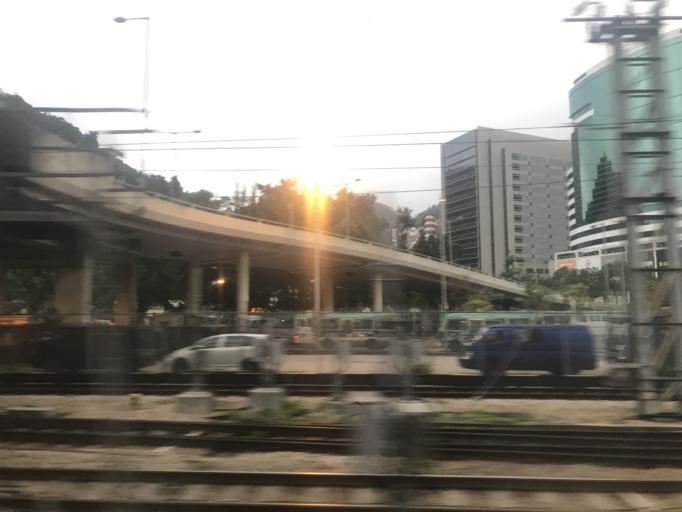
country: HK
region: Sha Tin
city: Sha Tin
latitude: 22.3838
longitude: 114.1882
